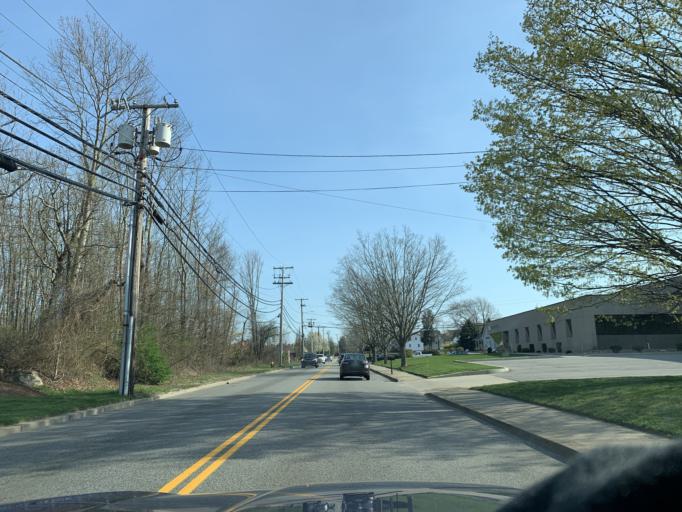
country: US
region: Rhode Island
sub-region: Providence County
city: Johnston
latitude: 41.7846
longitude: -71.5157
